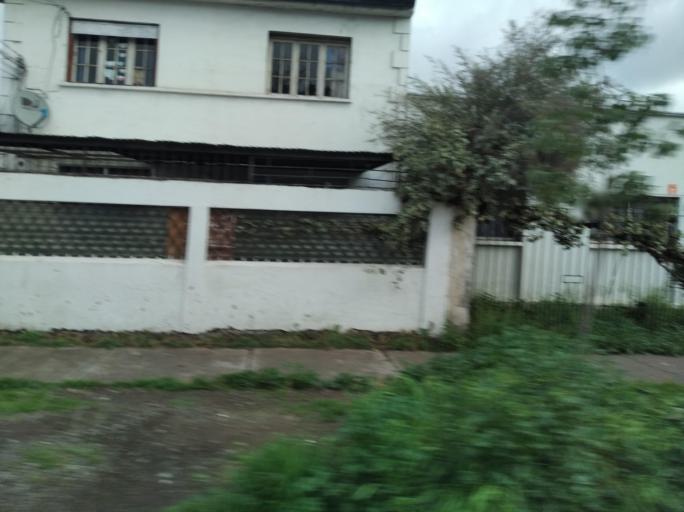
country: CL
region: Santiago Metropolitan
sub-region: Provincia de Santiago
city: Villa Presidente Frei, Nunoa, Santiago, Chile
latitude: -33.4881
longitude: -70.5935
